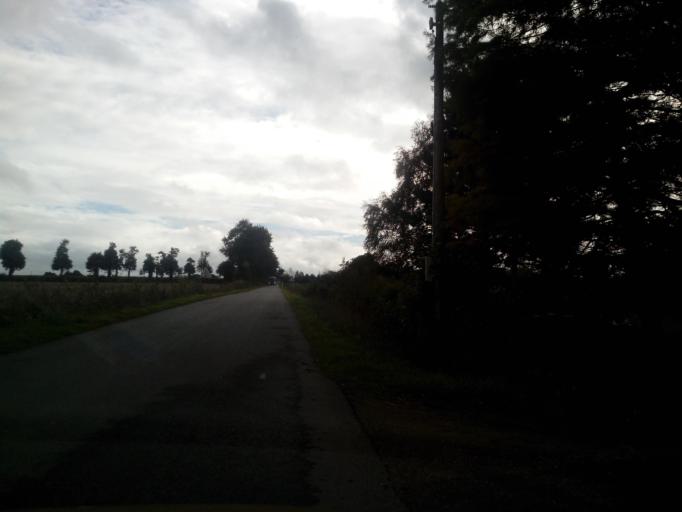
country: FR
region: Brittany
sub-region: Departement du Morbihan
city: Guilliers
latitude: 48.1148
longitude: -2.3837
